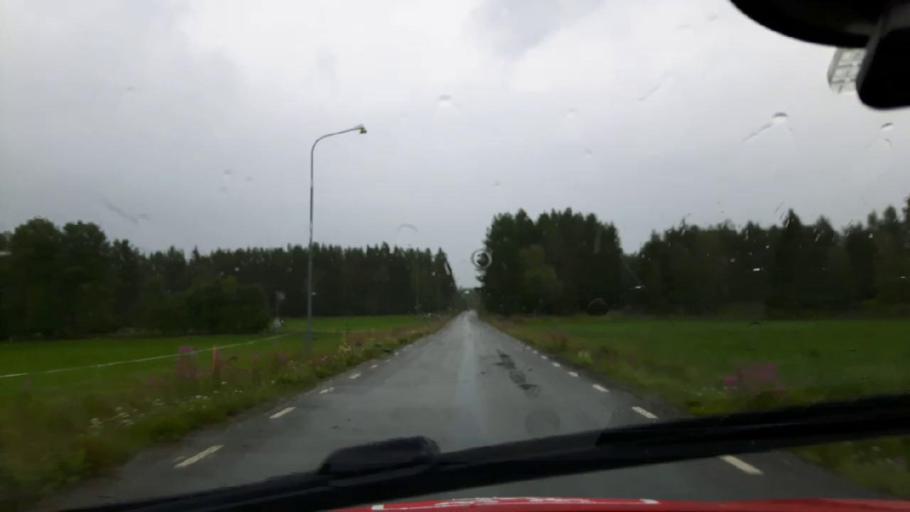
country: SE
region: Jaemtland
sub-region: OEstersunds Kommun
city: Brunflo
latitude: 62.9838
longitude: 14.8176
